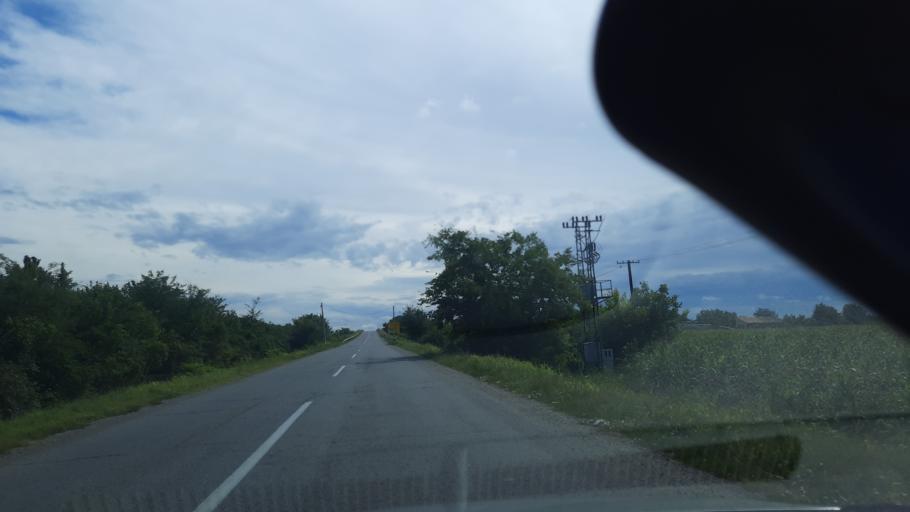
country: RS
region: Autonomna Pokrajina Vojvodina
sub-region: Sremski Okrug
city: Sremska Mitrovica
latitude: 45.0079
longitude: 19.6135
